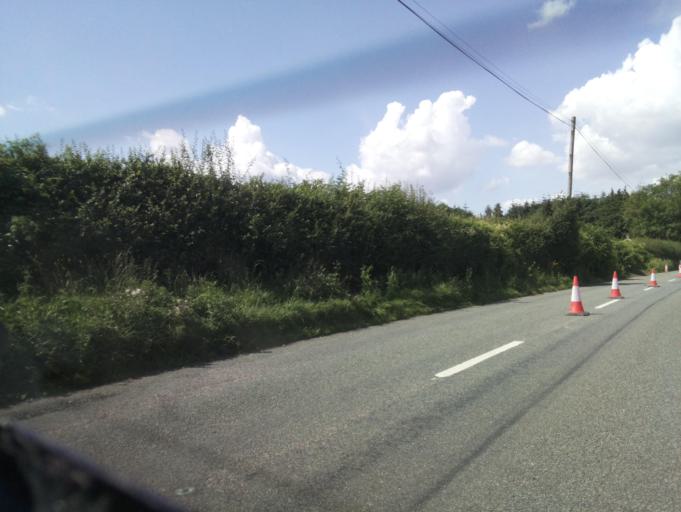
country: GB
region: England
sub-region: West Berkshire
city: Farnborough
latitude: 51.4882
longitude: -1.3647
